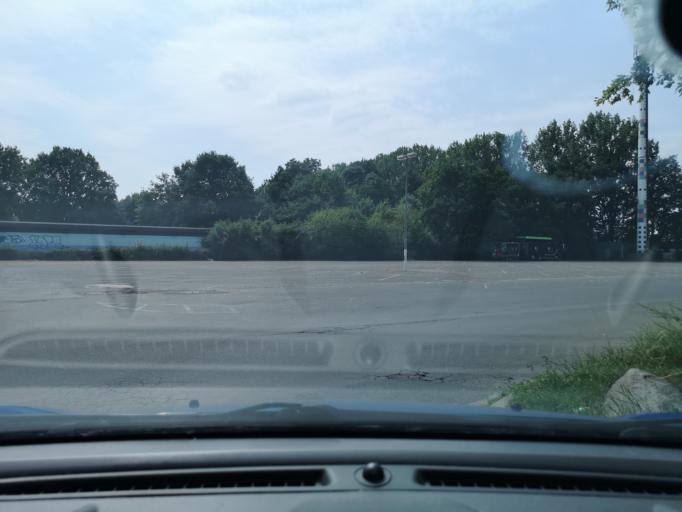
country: DE
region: Lower Saxony
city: Langenhagen
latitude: 52.4335
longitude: 9.6981
